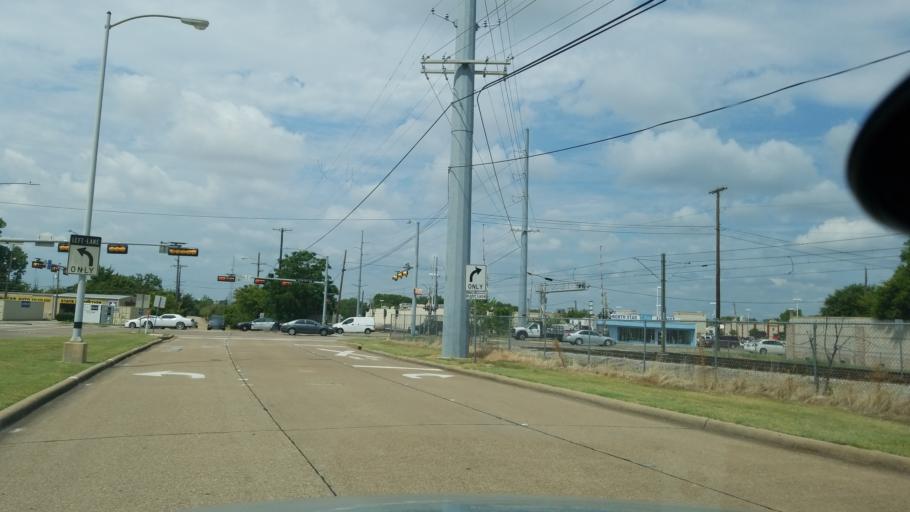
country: US
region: Texas
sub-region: Dallas County
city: Garland
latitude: 32.9140
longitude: -96.6473
